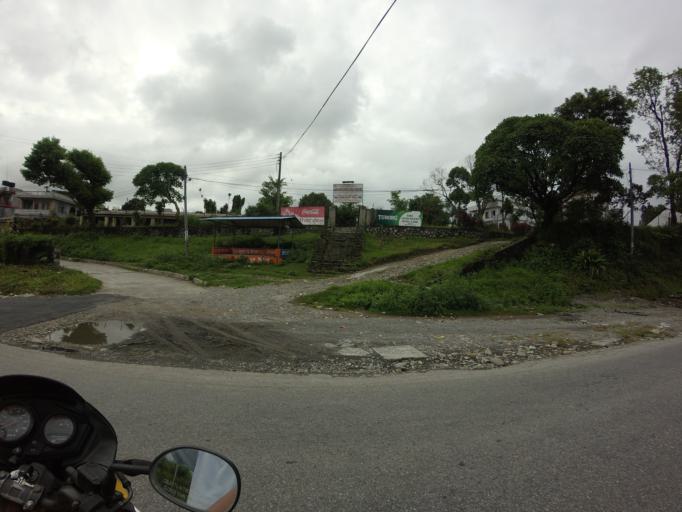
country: NP
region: Western Region
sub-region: Gandaki Zone
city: Pokhara
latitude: 28.2026
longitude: 83.9818
